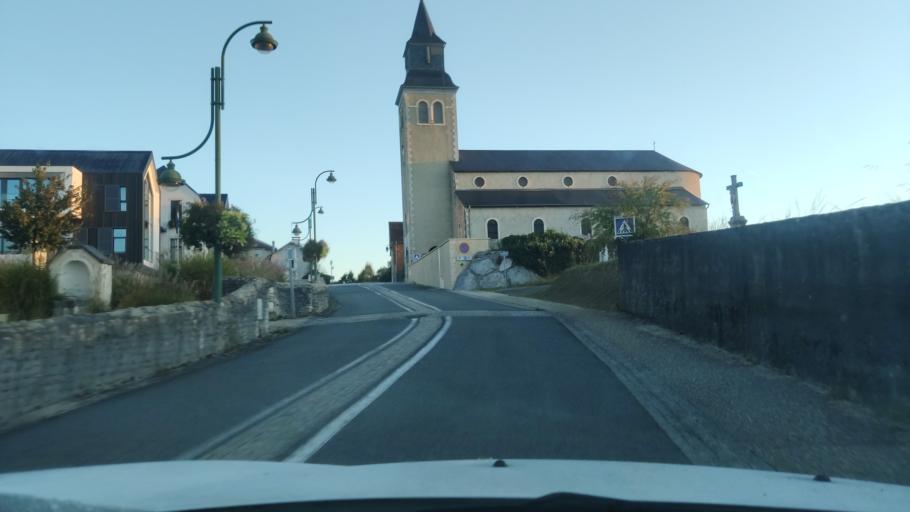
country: FR
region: Aquitaine
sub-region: Departement des Pyrenees-Atlantiques
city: Sauvagnon
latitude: 43.4024
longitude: -0.3871
